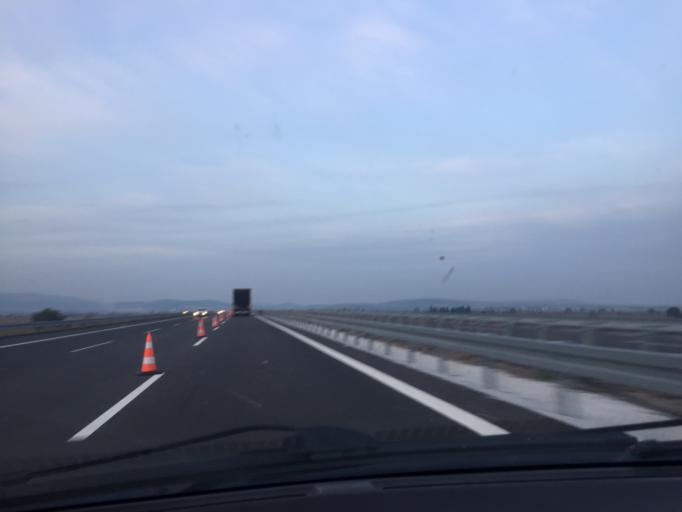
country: TR
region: Manisa
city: Halitpasa
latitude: 38.7358
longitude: 27.6570
